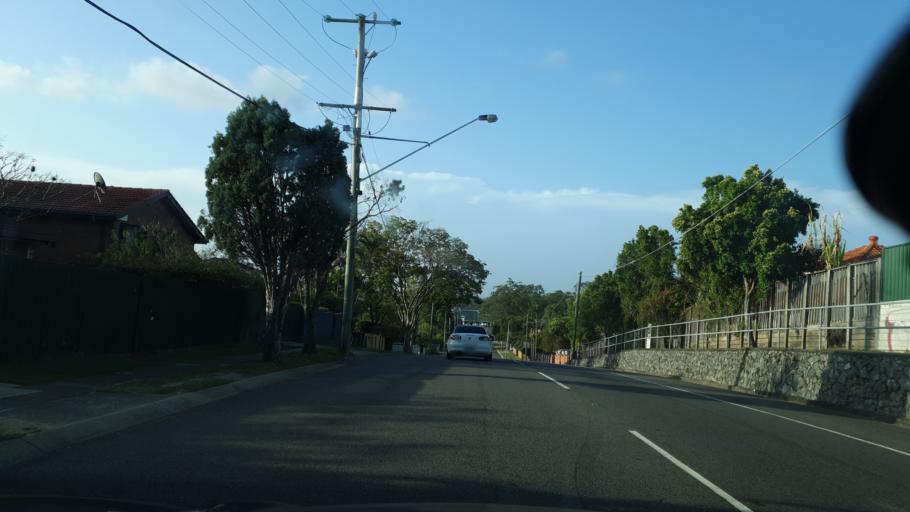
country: AU
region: Queensland
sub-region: Brisbane
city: Belmont
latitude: -27.4885
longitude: 153.1272
